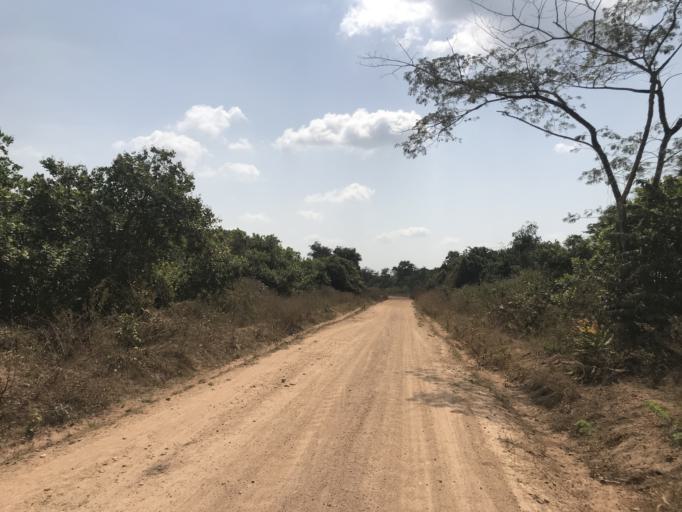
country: NG
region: Osun
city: Ifon
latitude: 7.9340
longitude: 4.4840
